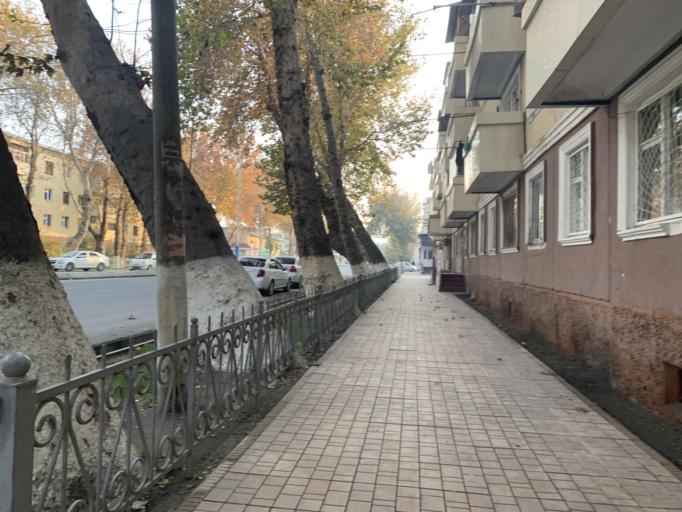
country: UZ
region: Fergana
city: Qo`qon
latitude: 40.5292
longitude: 70.9389
